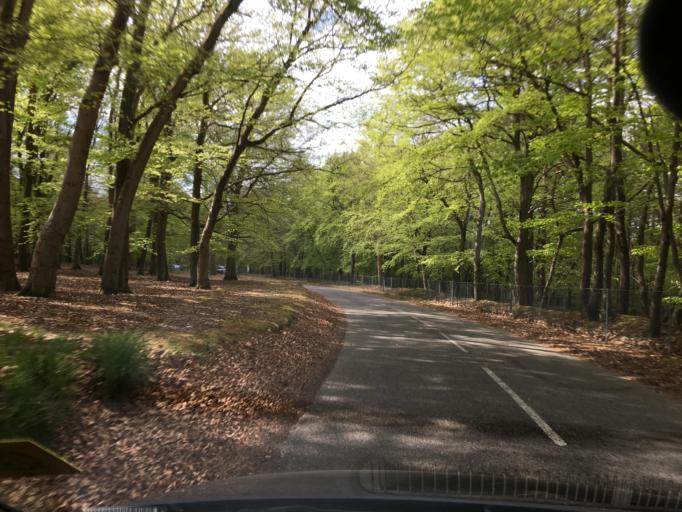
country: GB
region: England
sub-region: Hampshire
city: Aldershot
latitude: 51.2618
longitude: -0.7844
